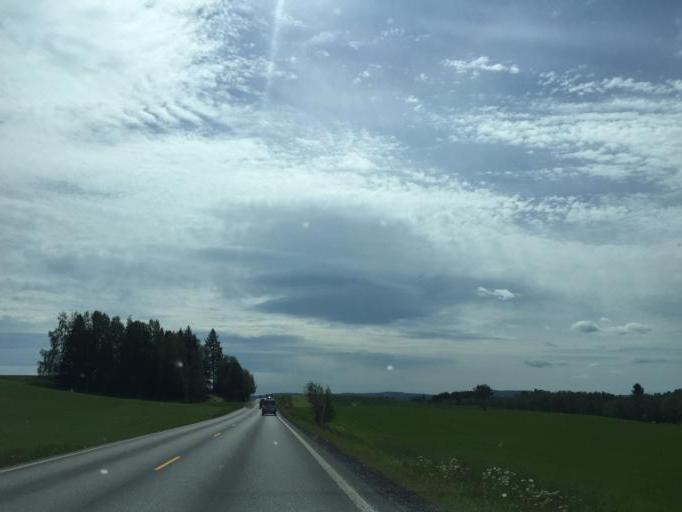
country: NO
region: Akershus
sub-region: Nes
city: Arnes
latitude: 60.1322
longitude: 11.4392
